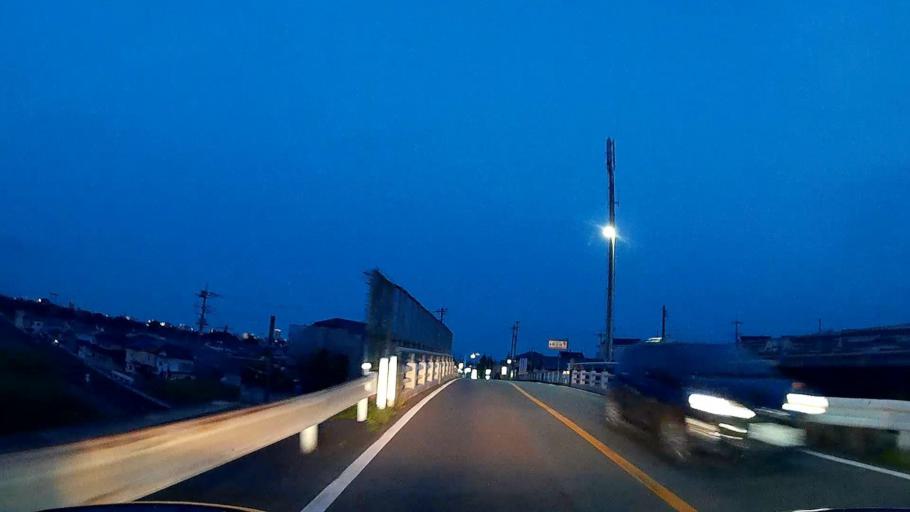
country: JP
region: Gunma
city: Takasaki
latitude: 36.3390
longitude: 138.9779
